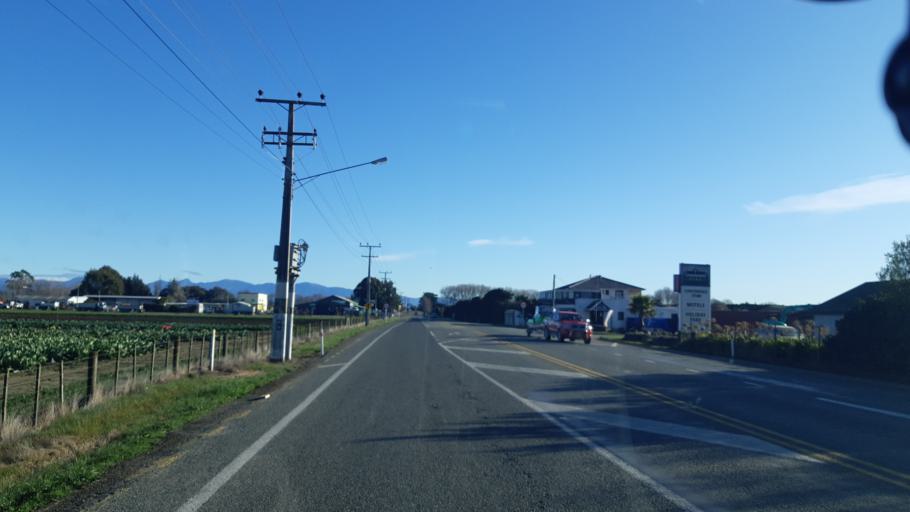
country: NZ
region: Tasman
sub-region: Tasman District
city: Richmond
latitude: -41.3157
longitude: 173.1349
